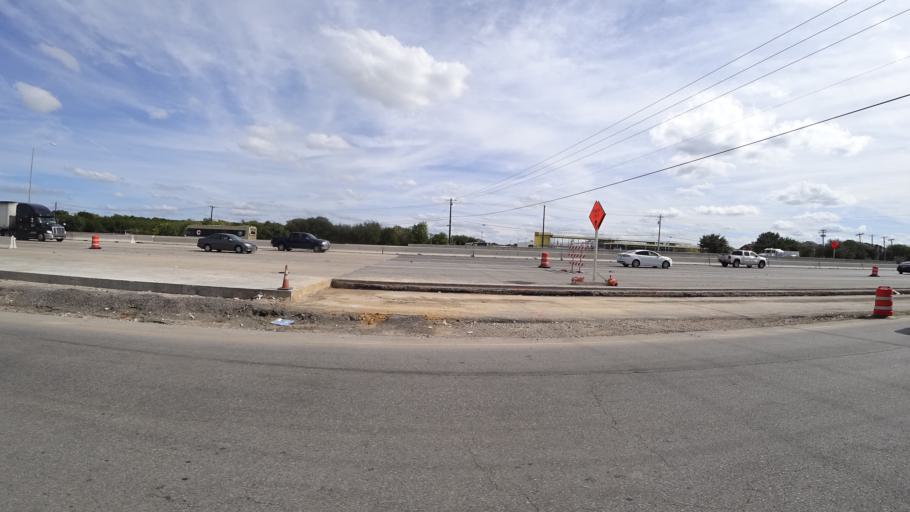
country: US
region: Texas
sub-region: Travis County
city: Onion Creek
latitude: 30.2012
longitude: -97.7623
